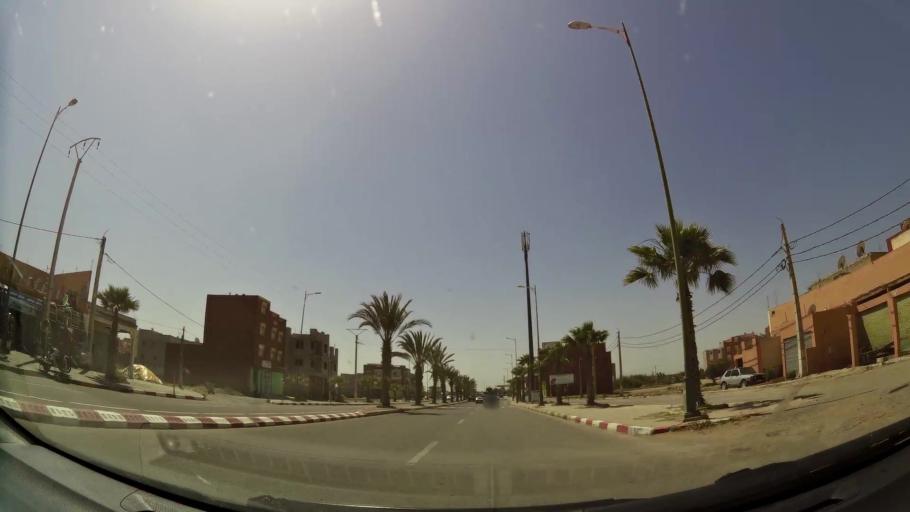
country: MA
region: Souss-Massa-Draa
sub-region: Inezgane-Ait Mellou
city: Inezgane
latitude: 30.3132
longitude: -9.5026
